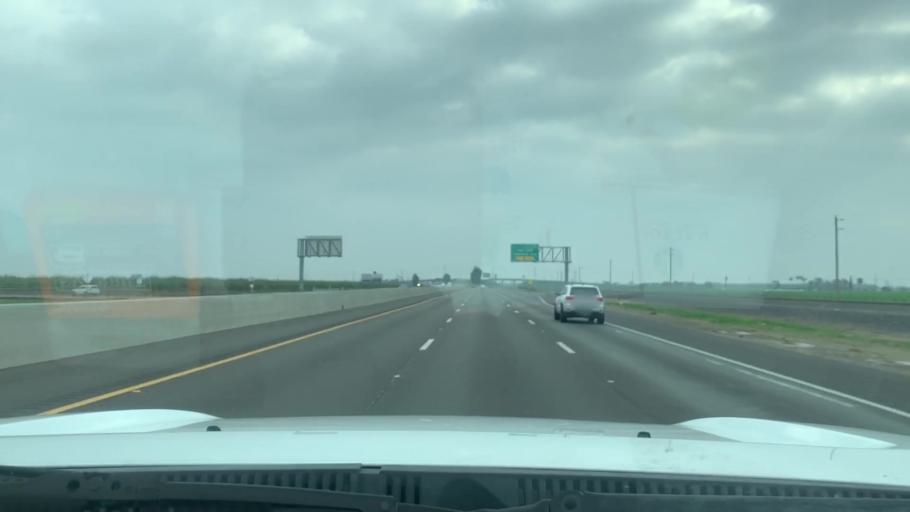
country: US
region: California
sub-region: Tulare County
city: Goshen
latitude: 36.3060
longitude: -119.3907
